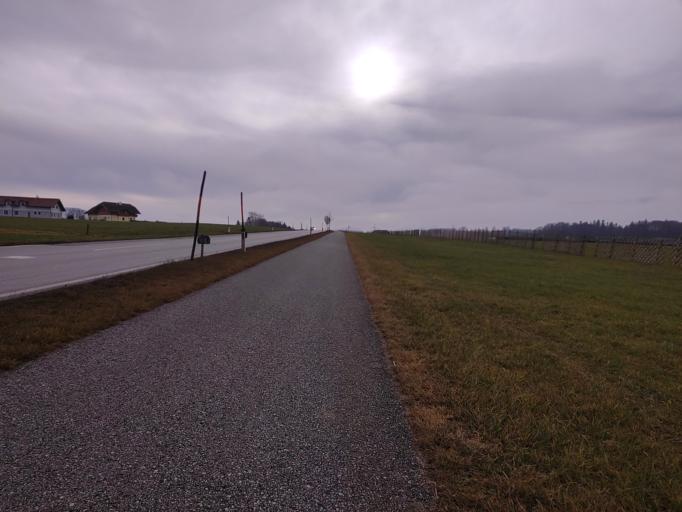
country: AT
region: Salzburg
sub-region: Politischer Bezirk Salzburg-Umgebung
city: Berndorf bei Salzburg
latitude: 47.9901
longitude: 13.0658
